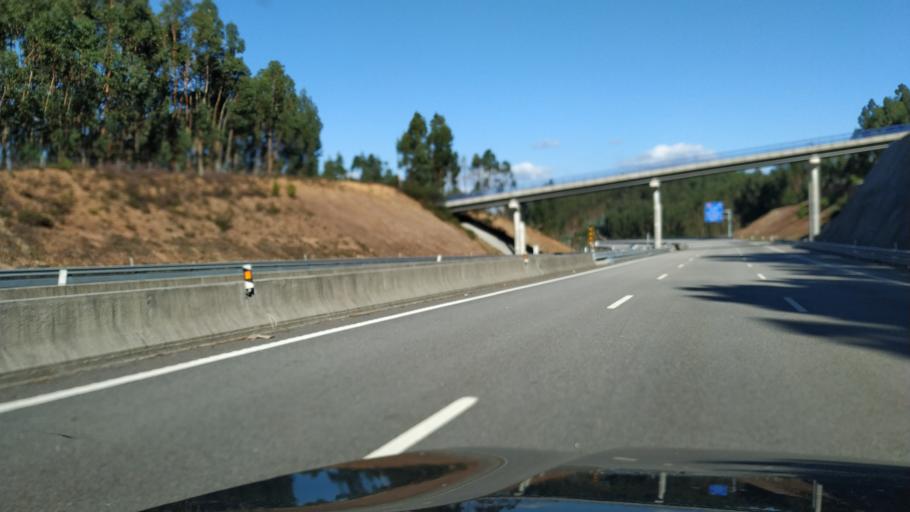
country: PT
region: Porto
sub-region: Vila Nova de Gaia
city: Sandim
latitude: 41.0208
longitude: -8.4787
